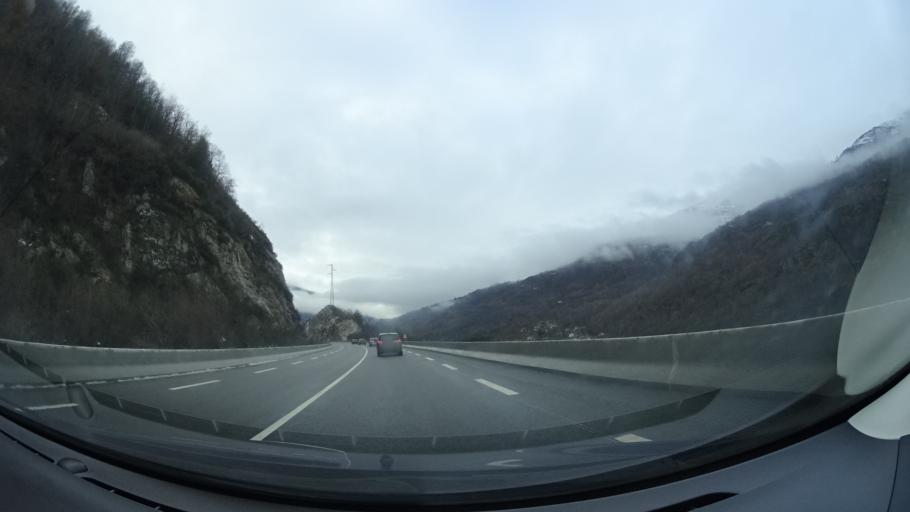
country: FR
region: Midi-Pyrenees
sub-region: Departement de l'Ariege
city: Ax-les-Thermes
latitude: 42.7237
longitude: 1.8305
